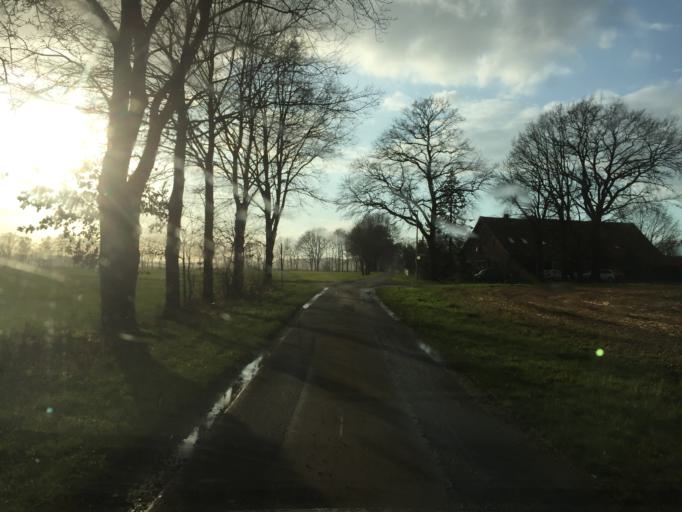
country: DE
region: Lower Saxony
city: Steyerberg
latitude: 52.5489
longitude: 9.0121
